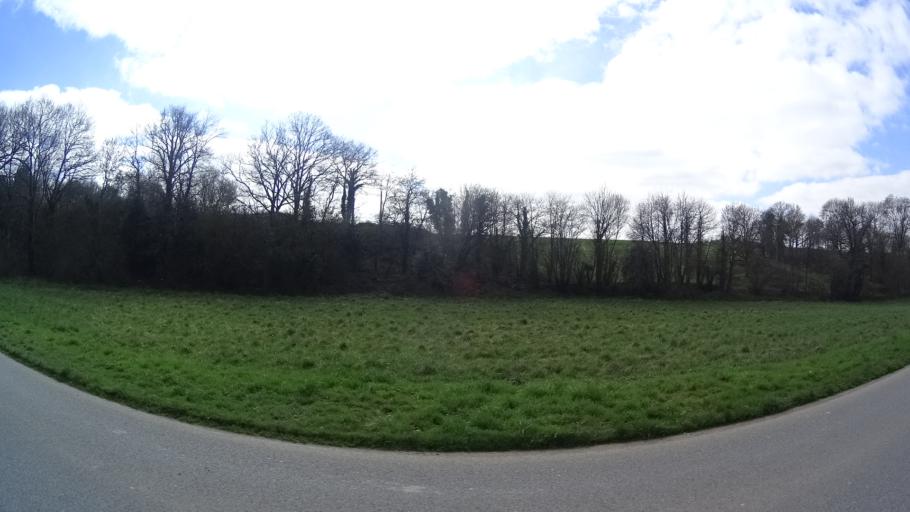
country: FR
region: Brittany
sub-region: Departement du Morbihan
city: Ruffiac
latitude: 47.8293
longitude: -2.3018
